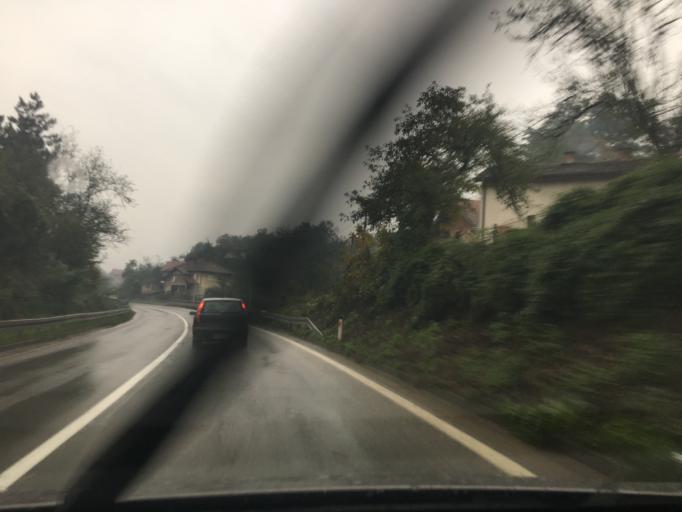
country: RS
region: Central Serbia
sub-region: Pcinjski Okrug
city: Vladicin Han
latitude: 42.8264
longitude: 22.1314
